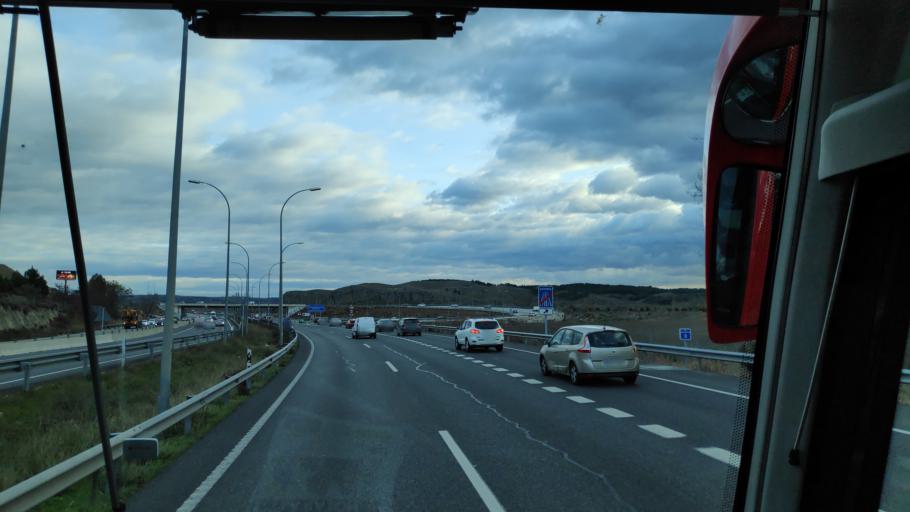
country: ES
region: Madrid
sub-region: Provincia de Madrid
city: Vaciamadrid
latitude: 40.3402
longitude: -3.5385
